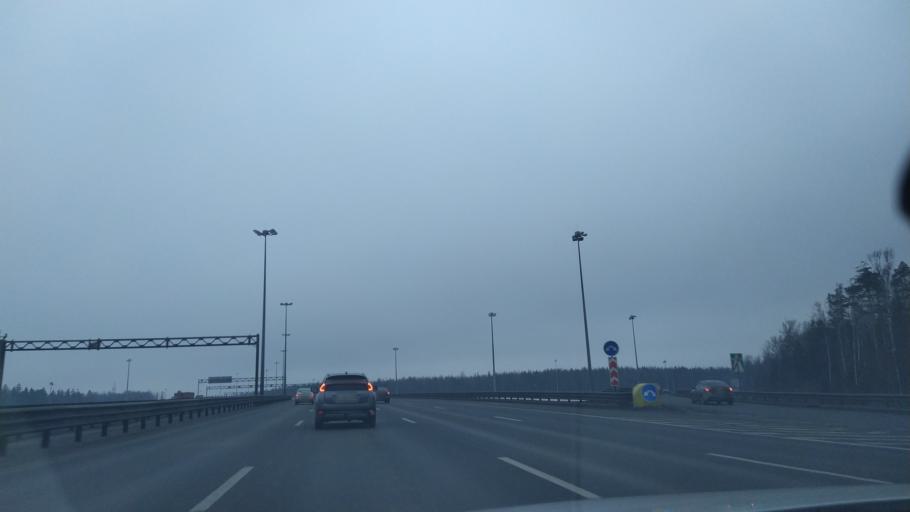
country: RU
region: St.-Petersburg
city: Krasnogvargeisky
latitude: 59.9489
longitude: 30.5429
